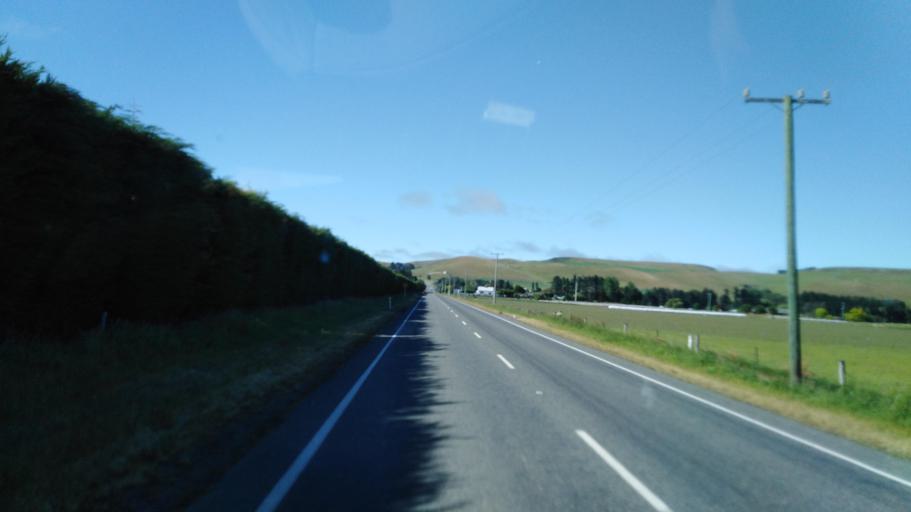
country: NZ
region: Canterbury
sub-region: Hurunui District
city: Amberley
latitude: -42.9601
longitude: 172.7082
